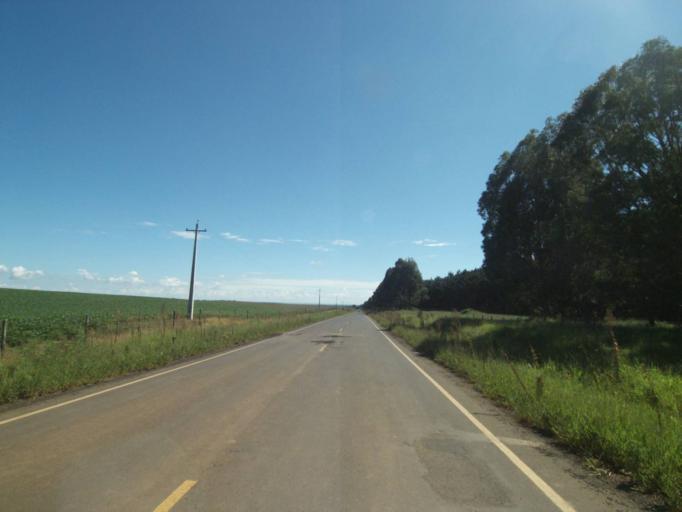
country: BR
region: Parana
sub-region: Pinhao
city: Pinhao
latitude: -25.8297
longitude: -52.0192
